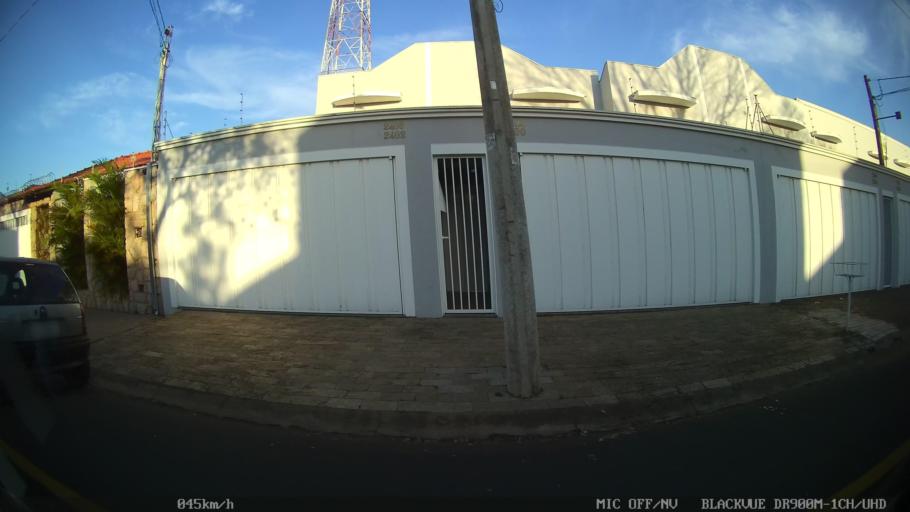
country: BR
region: Sao Paulo
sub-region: Franca
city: Franca
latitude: -20.5129
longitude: -47.3870
